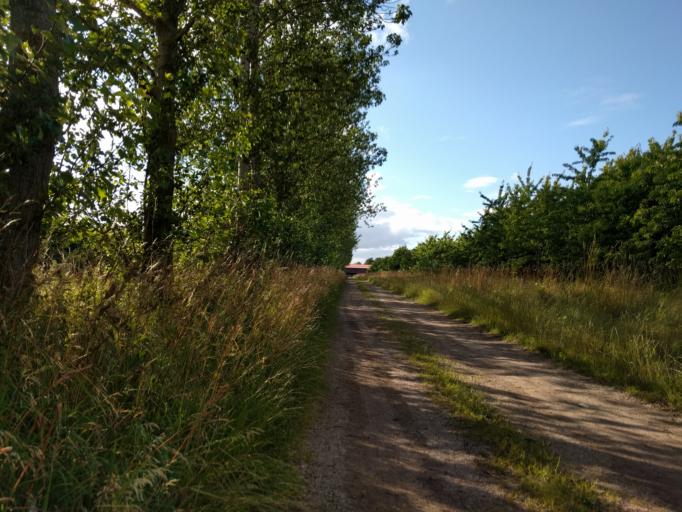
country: DK
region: South Denmark
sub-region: Kerteminde Kommune
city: Langeskov
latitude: 55.3900
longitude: 10.5484
